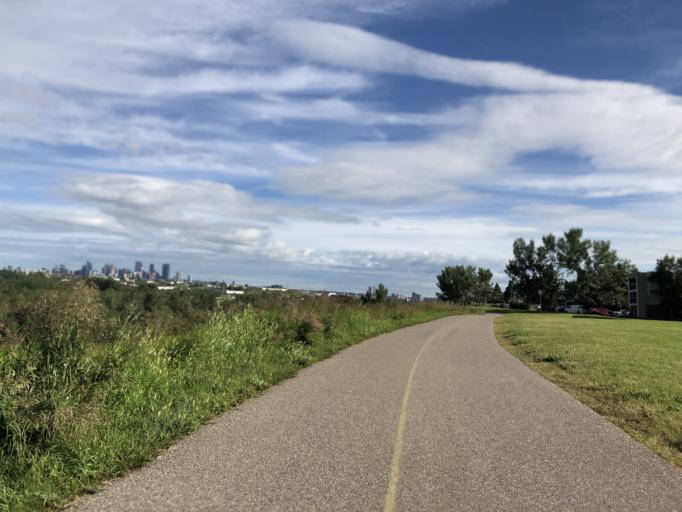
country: CA
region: Alberta
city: Calgary
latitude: 50.9953
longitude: -114.0231
